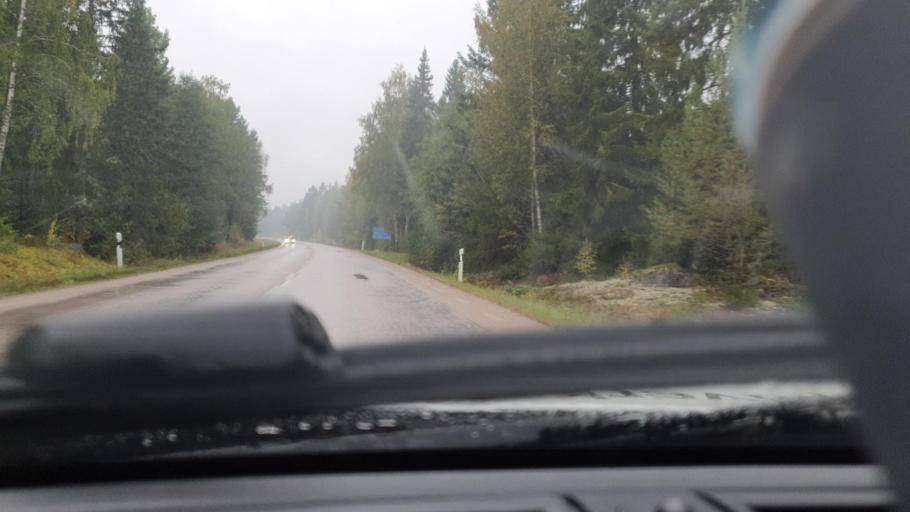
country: SE
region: Uppsala
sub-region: Tierps Kommun
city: Orbyhus
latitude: 60.2159
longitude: 17.7460
